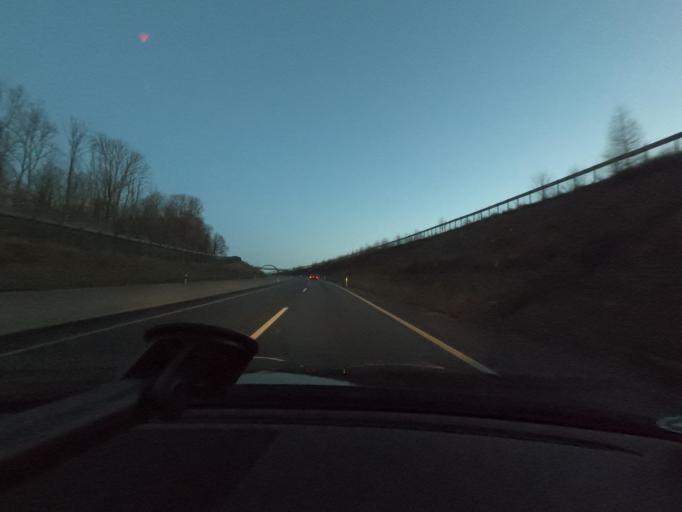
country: DE
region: Lower Saxony
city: Bad Lauterberg im Harz
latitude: 51.6192
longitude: 10.4343
